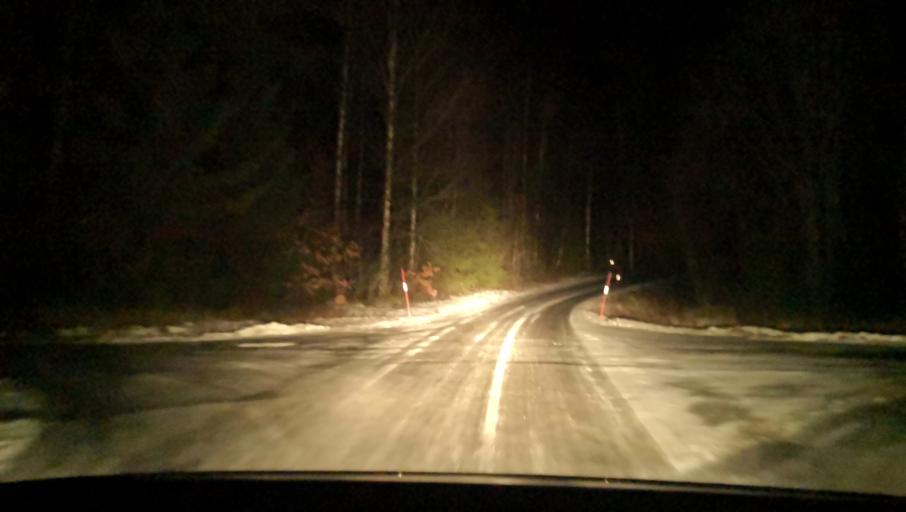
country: SE
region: Vaestmanland
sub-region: Vasteras
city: Tillberga
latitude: 59.6791
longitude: 16.6824
